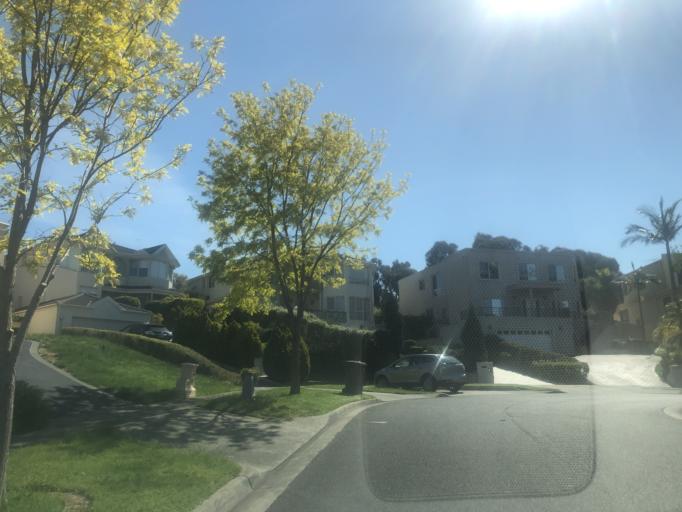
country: AU
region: Victoria
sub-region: Monash
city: Mulgrave
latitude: -37.9036
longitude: 145.1881
